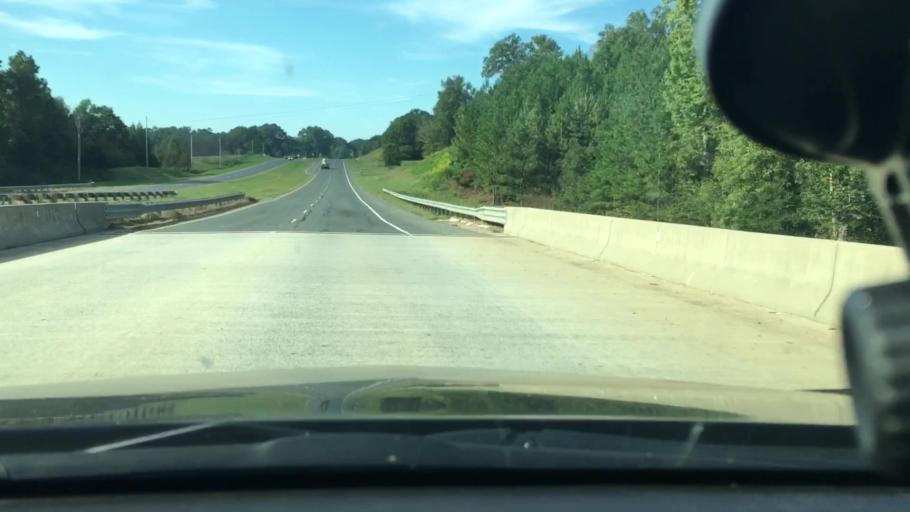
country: US
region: North Carolina
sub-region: Stanly County
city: Oakboro
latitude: 35.2802
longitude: -80.3032
